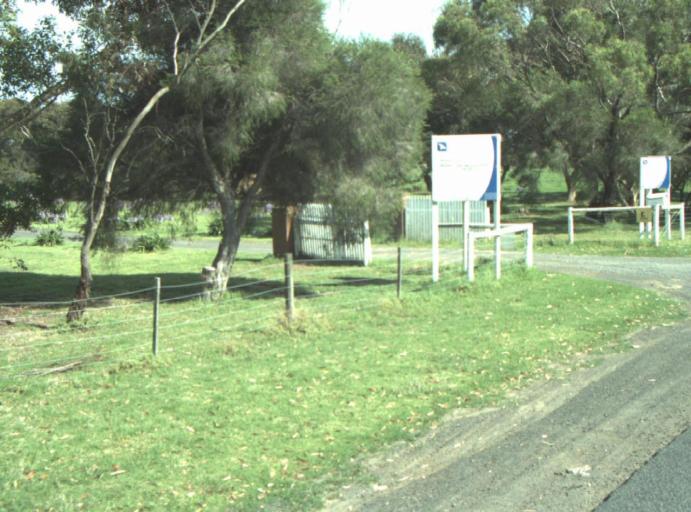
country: AU
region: Victoria
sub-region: Greater Geelong
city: Clifton Springs
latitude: -38.1797
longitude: 144.5511
